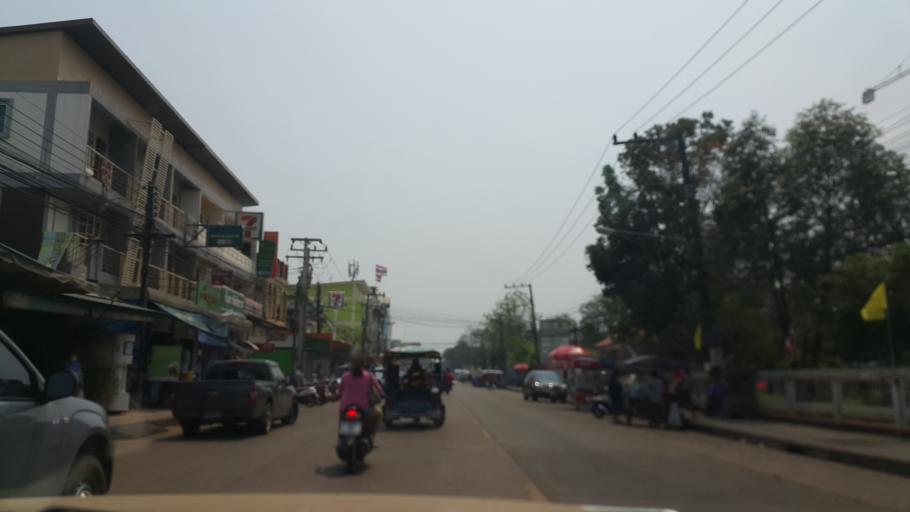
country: TH
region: Nakhon Phanom
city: Nakhon Phanom
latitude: 17.4141
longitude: 104.7781
